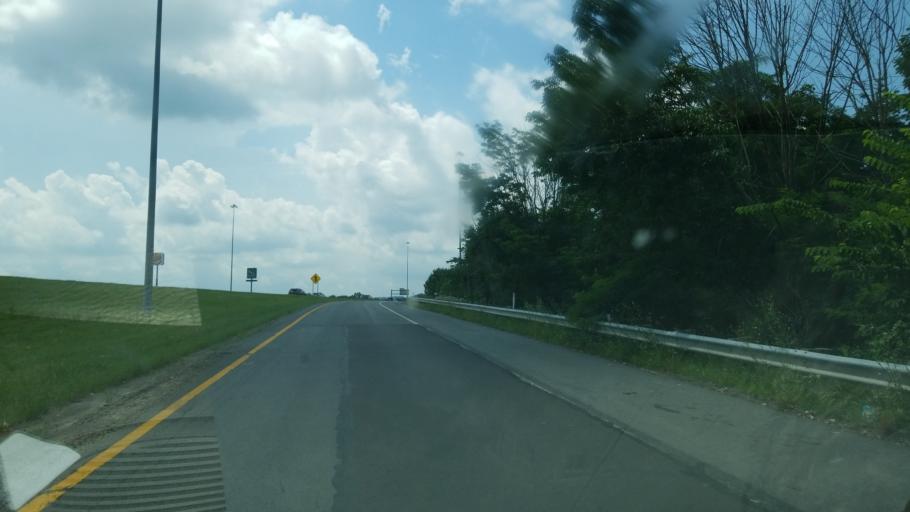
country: US
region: Ohio
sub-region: Richland County
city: Lexington
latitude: 40.6502
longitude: -82.5459
